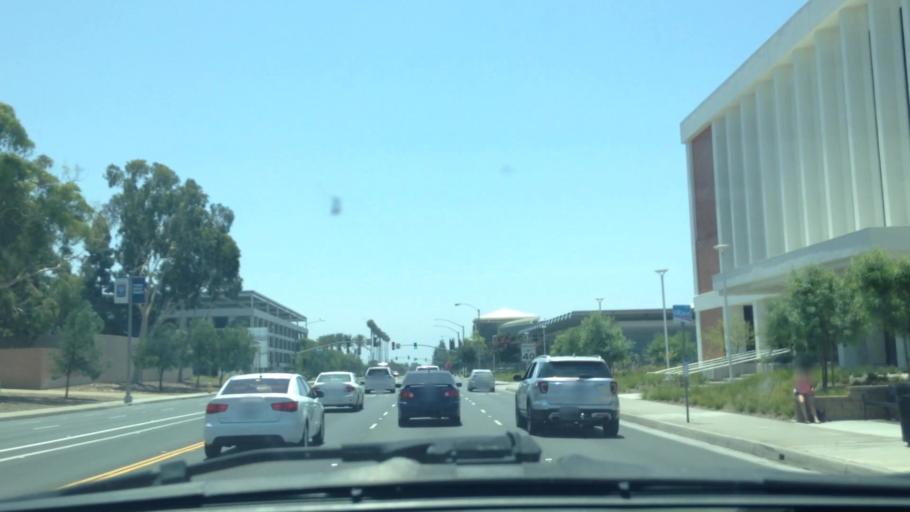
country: US
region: California
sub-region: Orange County
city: Placentia
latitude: 33.8812
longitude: -117.8898
